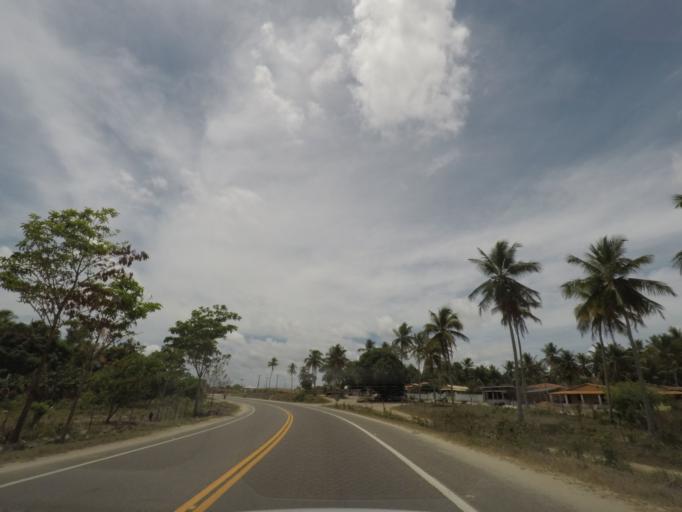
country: BR
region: Bahia
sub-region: Conde
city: Conde
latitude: -11.7926
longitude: -37.6265
